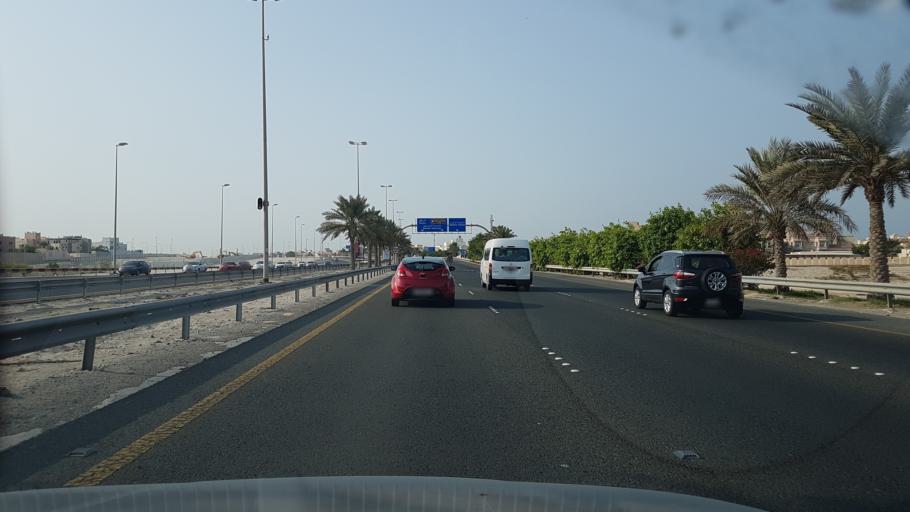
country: BH
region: Central Governorate
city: Madinat Hamad
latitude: 26.1316
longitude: 50.5084
